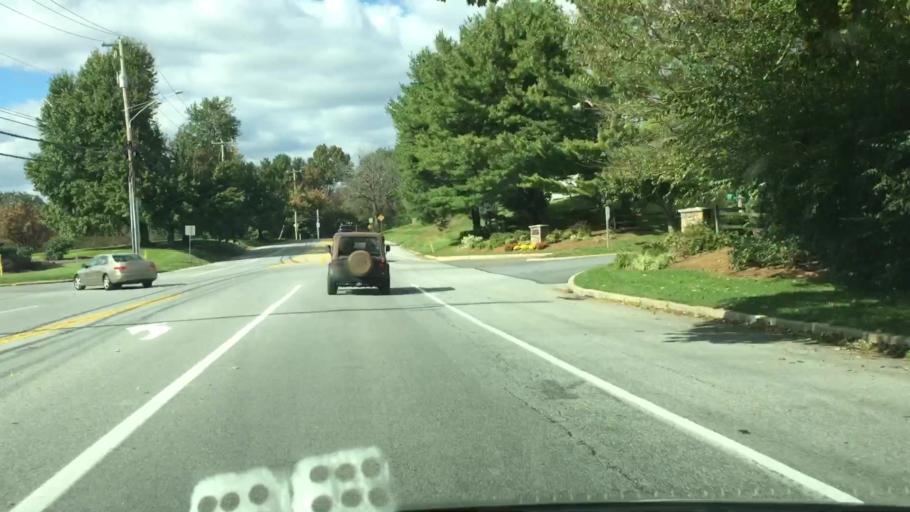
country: US
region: Pennsylvania
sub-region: Chester County
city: West Chester
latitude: 39.9909
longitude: -75.5562
